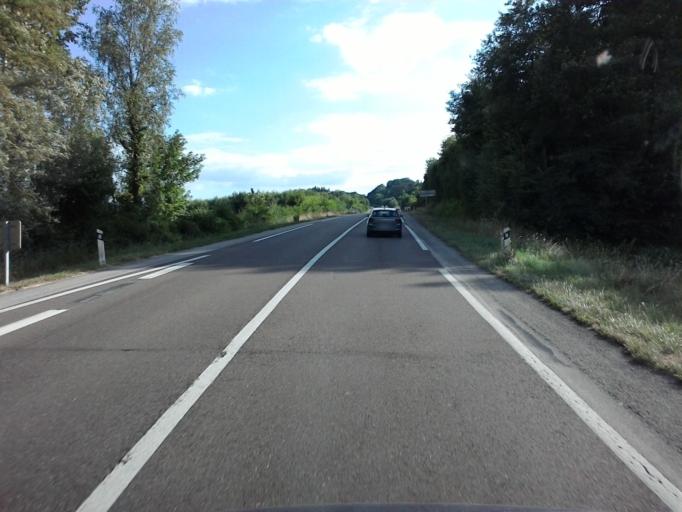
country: FR
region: Franche-Comte
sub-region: Departement de la Haute-Saone
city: Luxeuil-les-Bains
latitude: 47.7567
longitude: 6.3372
